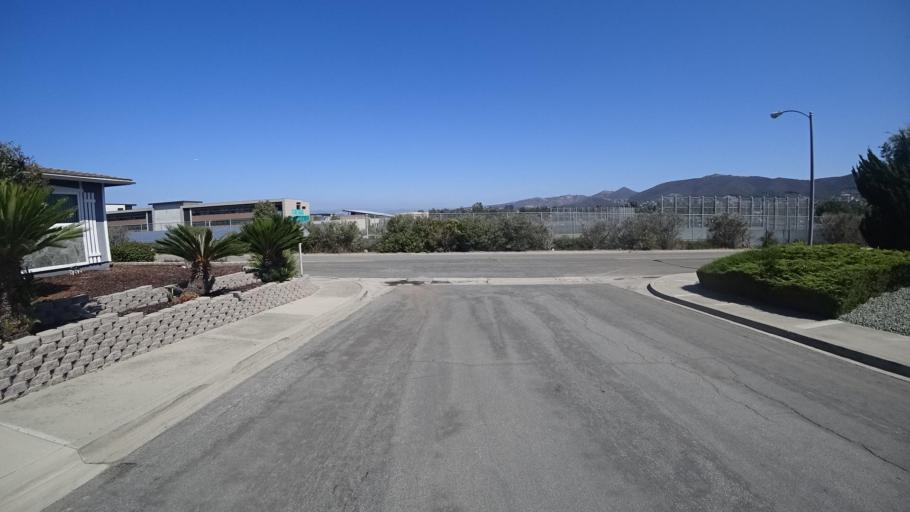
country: US
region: California
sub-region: San Diego County
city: Lake San Marcos
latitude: 33.1284
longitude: -117.2085
